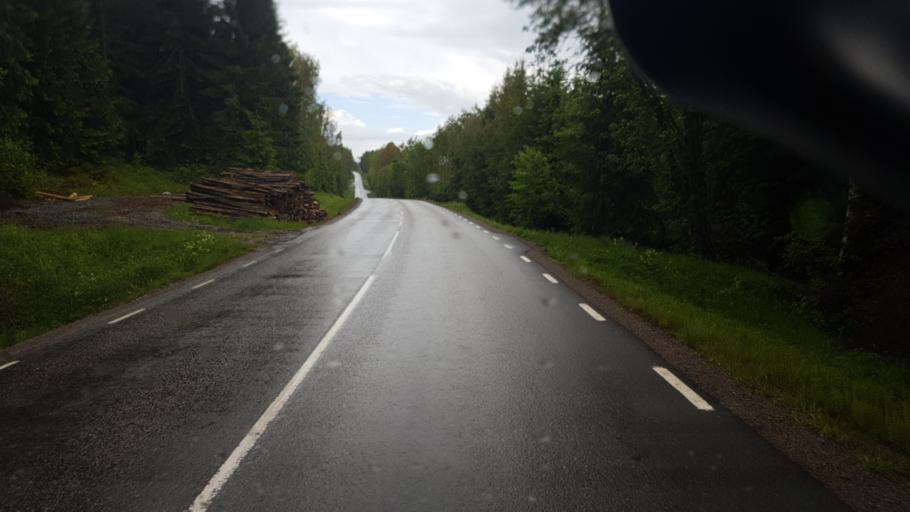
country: SE
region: Vaermland
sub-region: Eda Kommun
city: Amotfors
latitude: 59.7313
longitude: 12.4179
